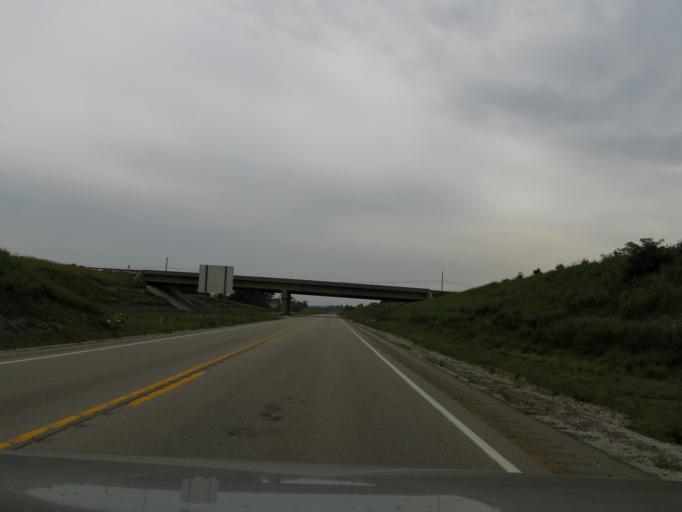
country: US
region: Ohio
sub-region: Brown County
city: Aberdeen
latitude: 38.6109
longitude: -83.8334
